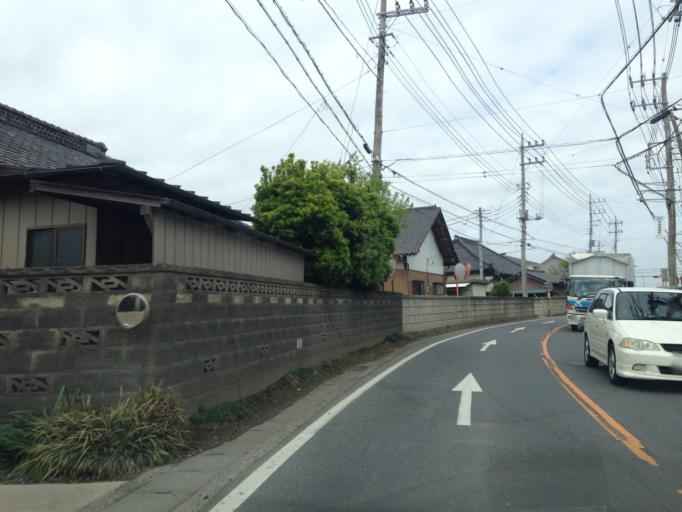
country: JP
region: Ibaraki
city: Tsukuba
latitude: 36.1356
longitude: 140.0656
